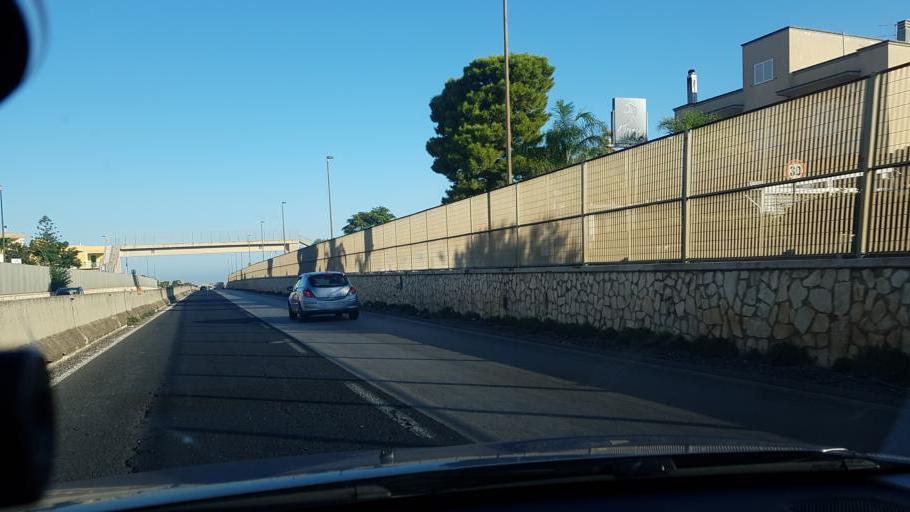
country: IT
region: Apulia
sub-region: Provincia di Brindisi
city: Fasano
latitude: 40.8829
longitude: 17.3370
